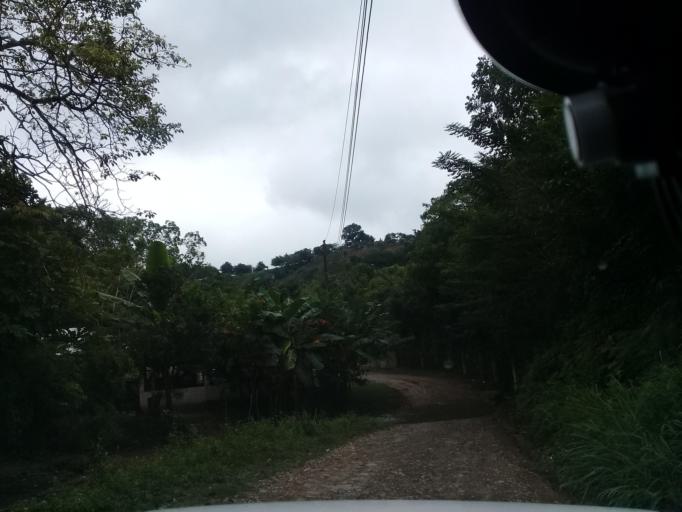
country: MX
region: Veracruz
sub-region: Chalma
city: San Pedro Coyutla
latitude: 21.2381
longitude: -98.4261
